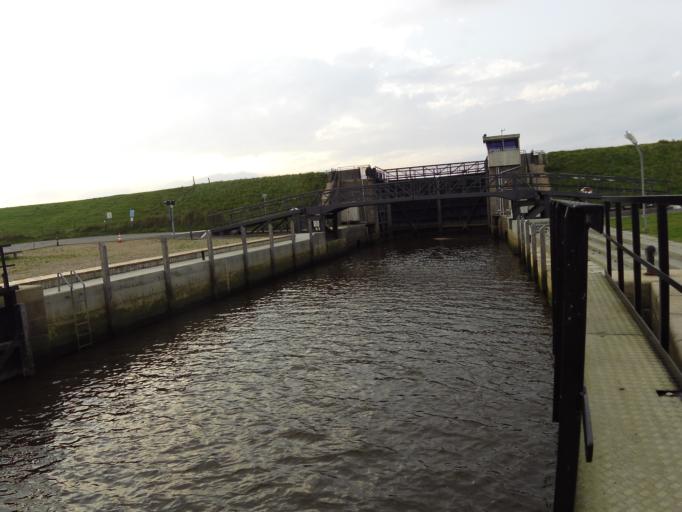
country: DK
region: South Denmark
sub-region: Esbjerg Kommune
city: Ribe
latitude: 55.3398
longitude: 8.6768
